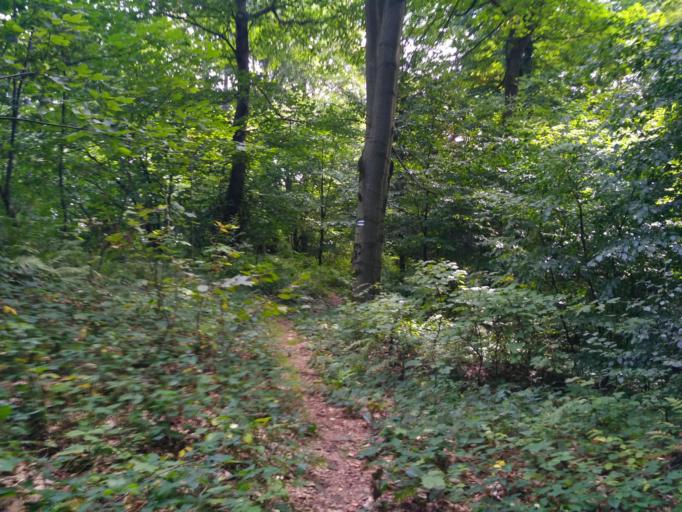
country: PL
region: Subcarpathian Voivodeship
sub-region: Powiat strzyzowski
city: Frysztak
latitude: 49.8868
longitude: 21.5423
